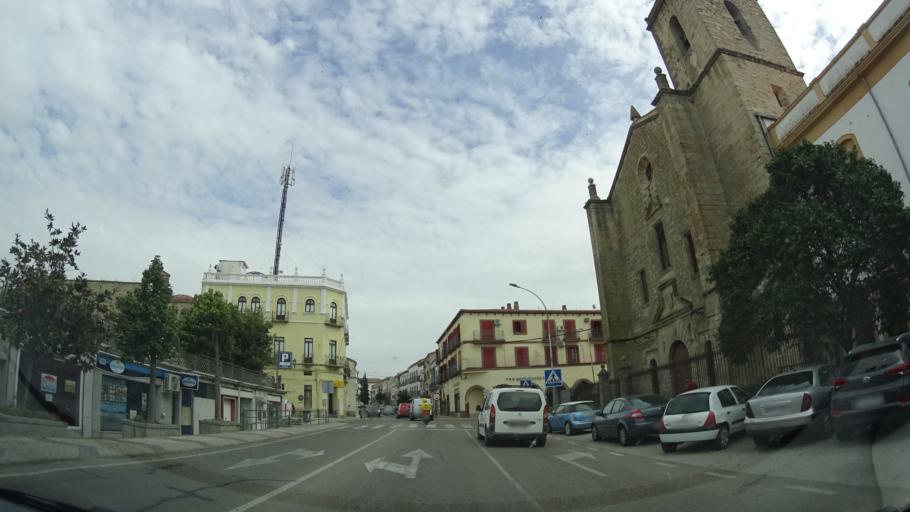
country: ES
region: Extremadura
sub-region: Provincia de Caceres
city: Trujillo
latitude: 39.4569
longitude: -5.8822
